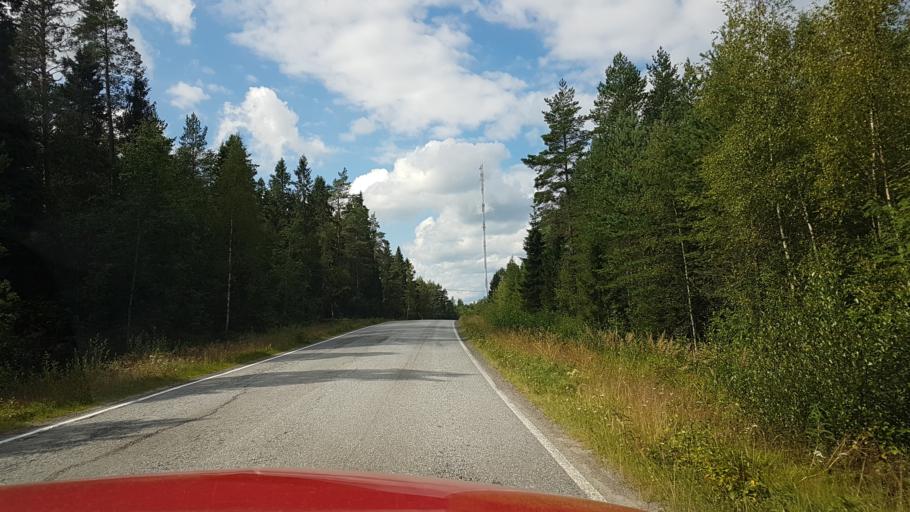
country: FI
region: Northern Ostrobothnia
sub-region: Ylivieska
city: Himanka
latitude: 64.0664
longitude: 23.6824
